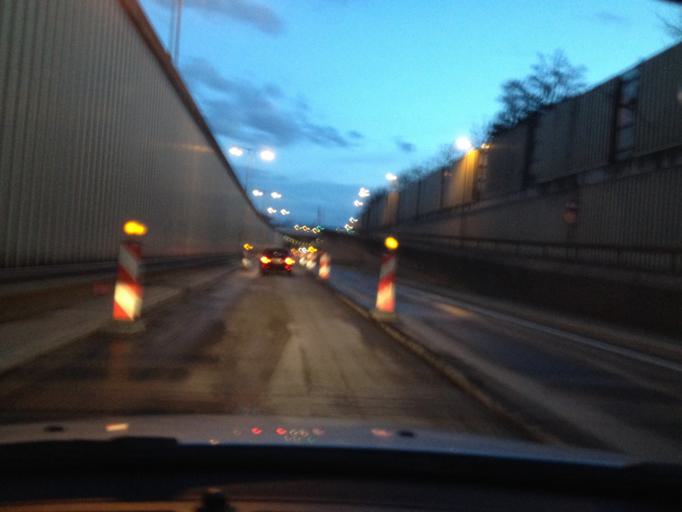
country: DE
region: Bavaria
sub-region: Swabia
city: Stadtbergen
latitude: 48.3751
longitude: 10.8563
